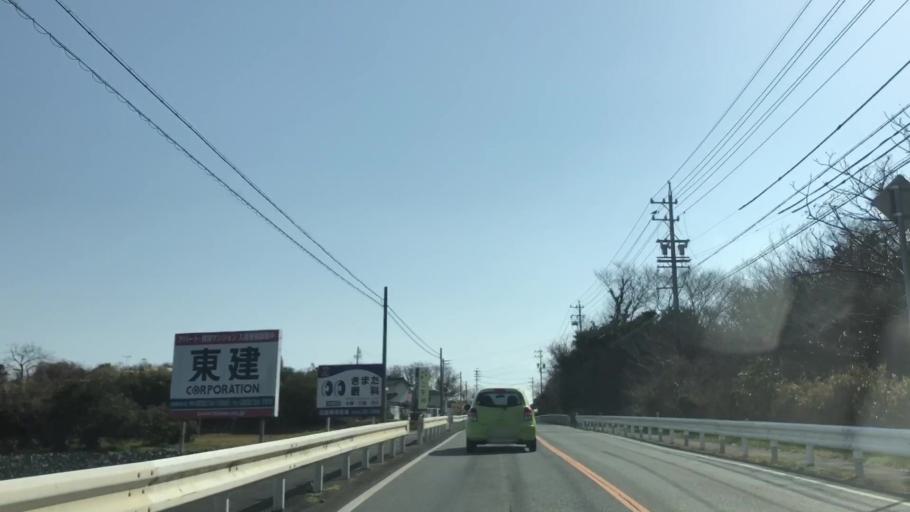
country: JP
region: Aichi
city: Tahara
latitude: 34.6880
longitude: 137.2806
